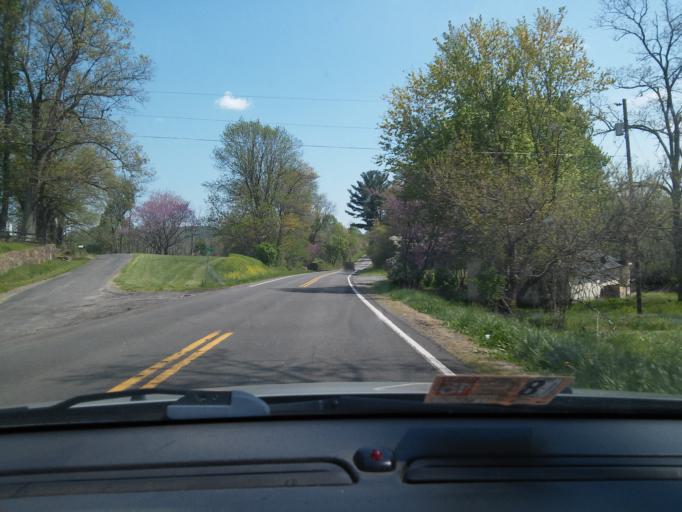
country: US
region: Virginia
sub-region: Warren County
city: Apple Mountain Lake
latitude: 38.8302
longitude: -78.1144
